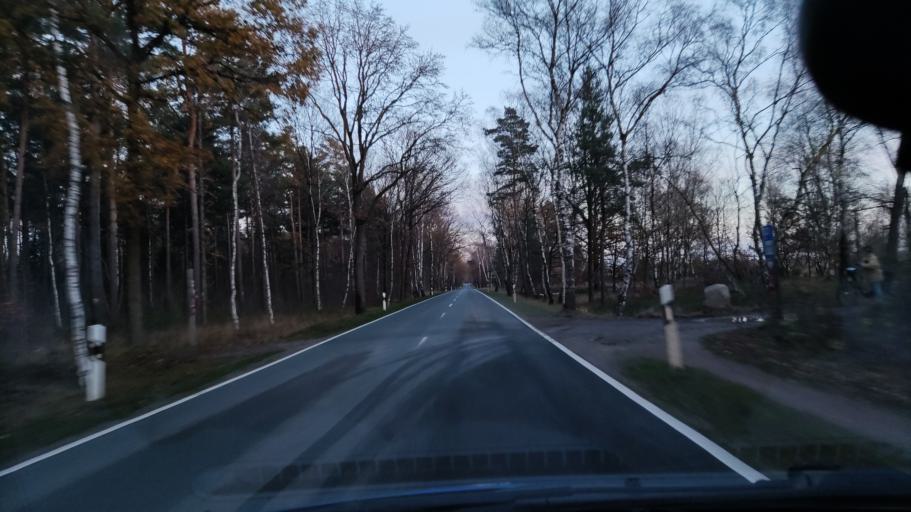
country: DE
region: Lower Saxony
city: Schneverdingen
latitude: 53.1255
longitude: 9.8178
